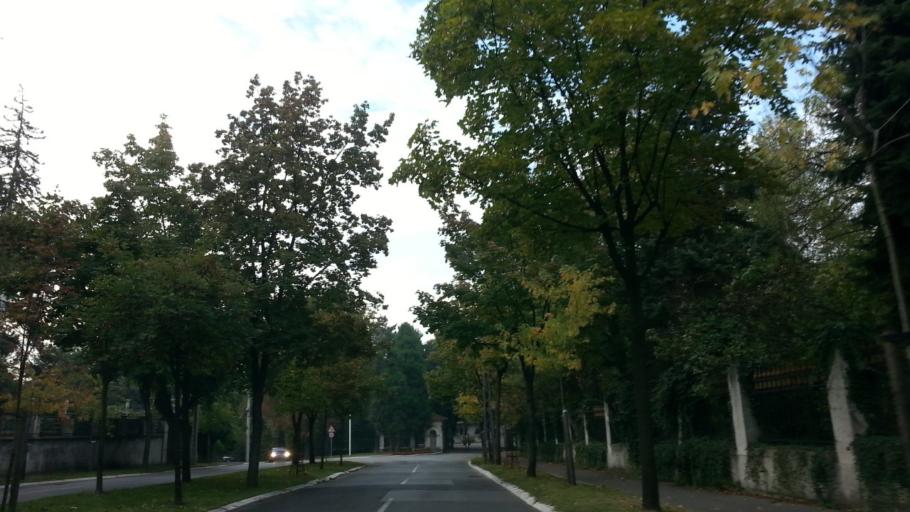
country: RS
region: Central Serbia
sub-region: Belgrade
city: Savski Venac
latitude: 44.7712
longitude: 20.4541
